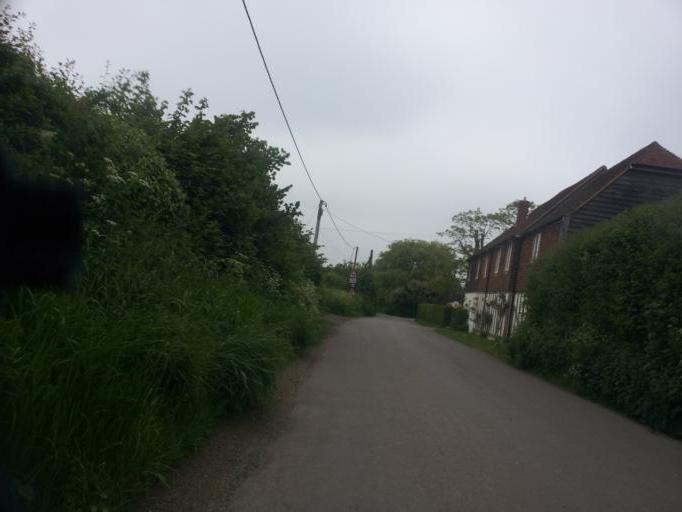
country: GB
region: England
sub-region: Kent
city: Maidstone
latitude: 51.2481
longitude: 0.5733
